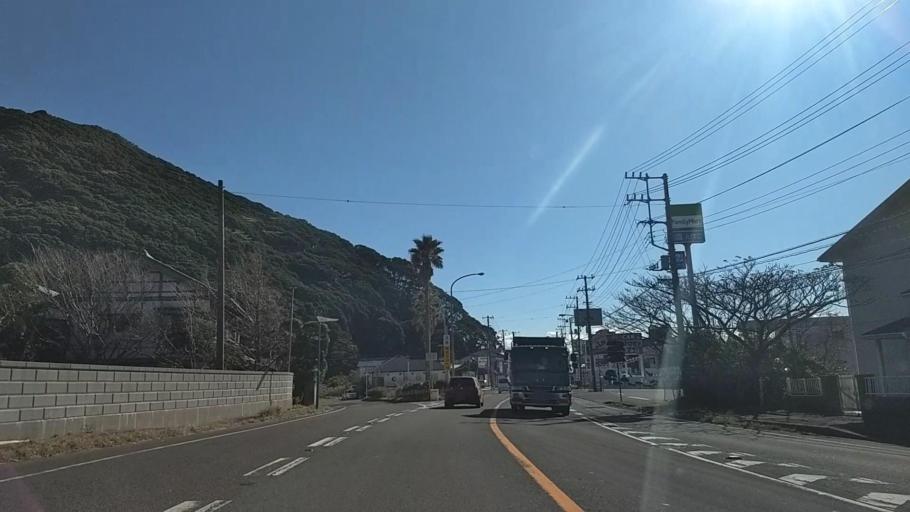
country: JP
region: Chiba
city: Kawaguchi
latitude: 35.1239
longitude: 140.1724
